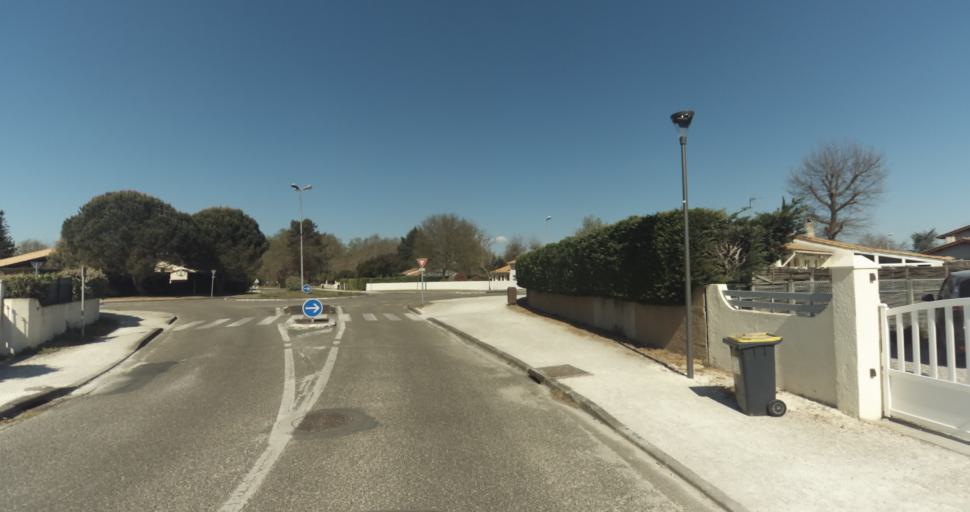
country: FR
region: Aquitaine
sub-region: Departement de la Gironde
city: Martignas-sur-Jalle
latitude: 44.8046
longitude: -0.7853
